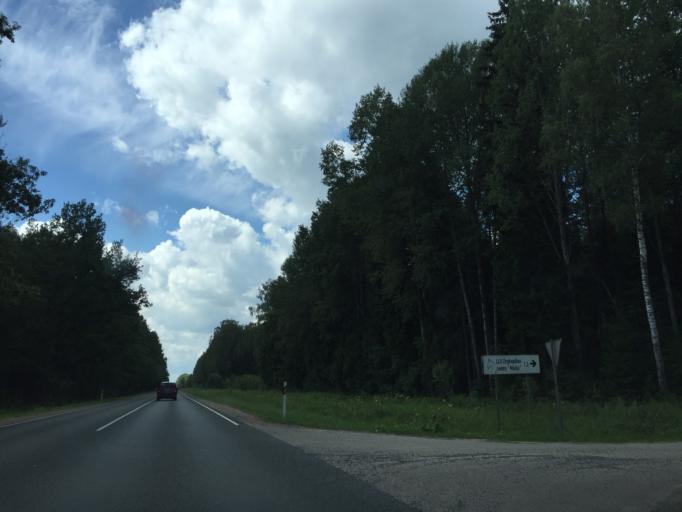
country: LV
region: Ozolnieku
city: Ozolnieki
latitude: 56.7008
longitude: 23.8118
